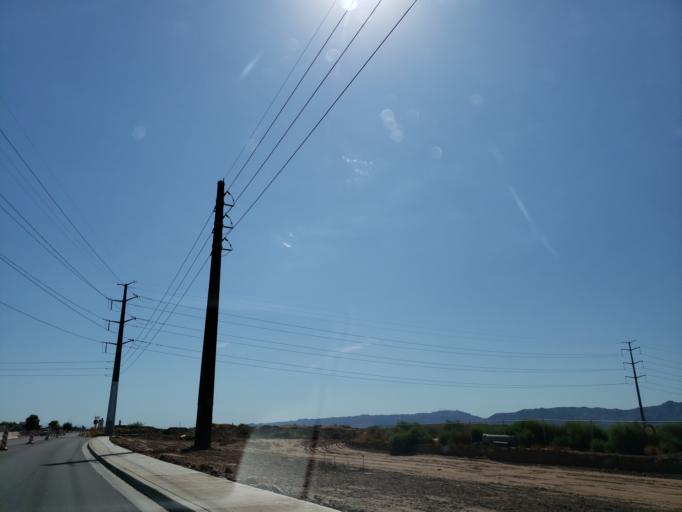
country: US
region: Arizona
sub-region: Maricopa County
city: Laveen
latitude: 33.4079
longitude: -112.1878
